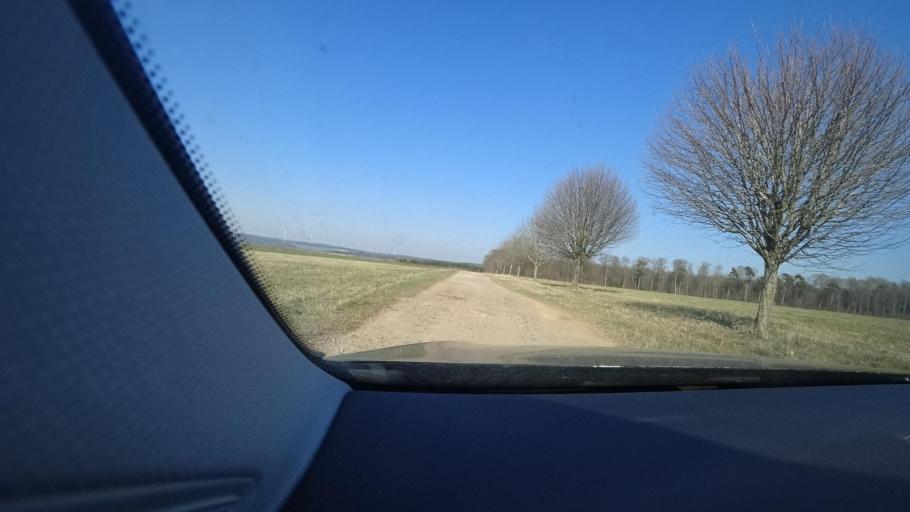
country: DE
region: Rheinland-Pfalz
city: Schnorbach
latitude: 49.9952
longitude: 7.6146
